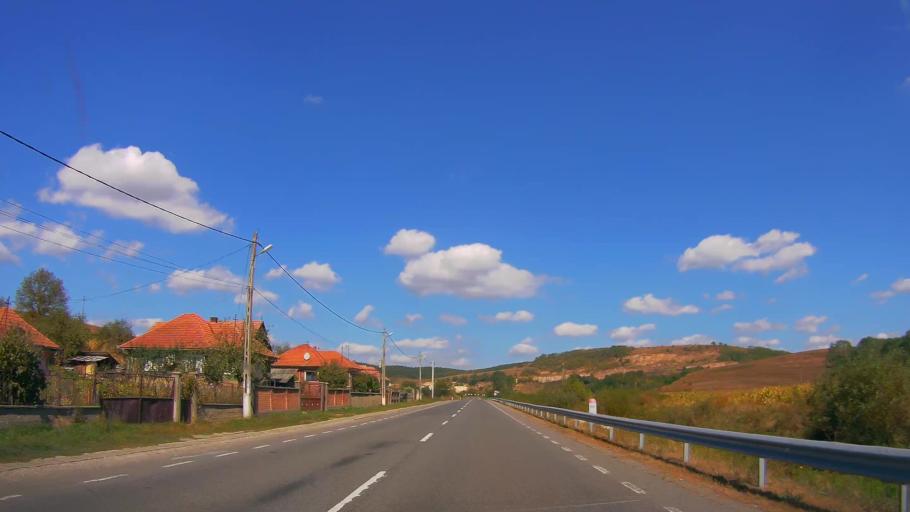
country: RO
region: Cluj
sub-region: Comuna Sanpaul
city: Sanpaul
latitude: 46.8774
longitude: 23.4183
